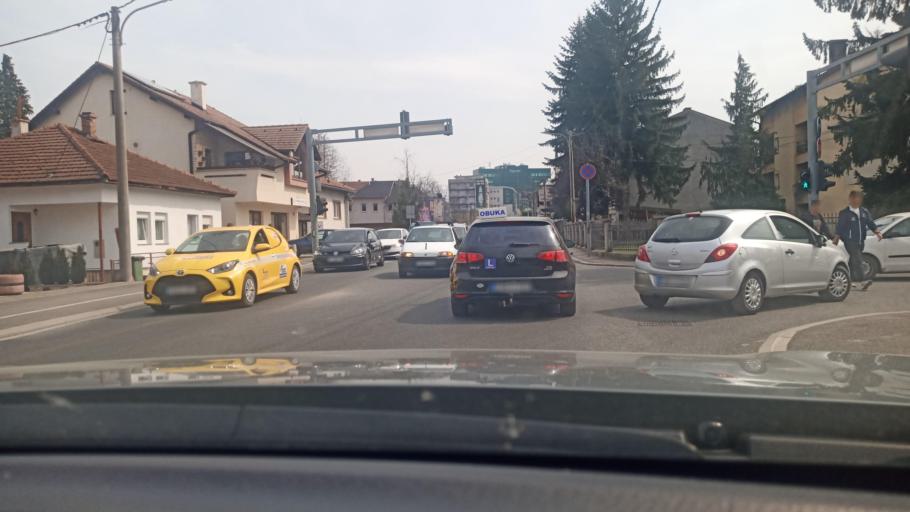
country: BA
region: Federation of Bosnia and Herzegovina
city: Bihac
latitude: 44.8180
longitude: 15.8658
